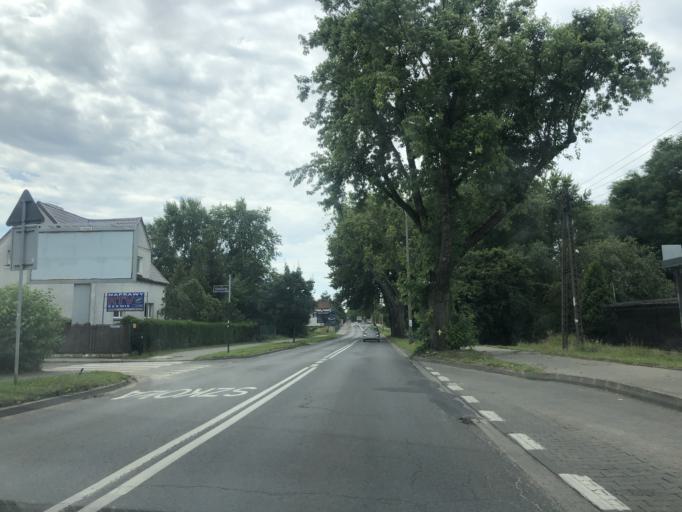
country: PL
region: Greater Poland Voivodeship
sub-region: Powiat poznanski
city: Lubon
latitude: 52.3657
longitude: 16.8947
